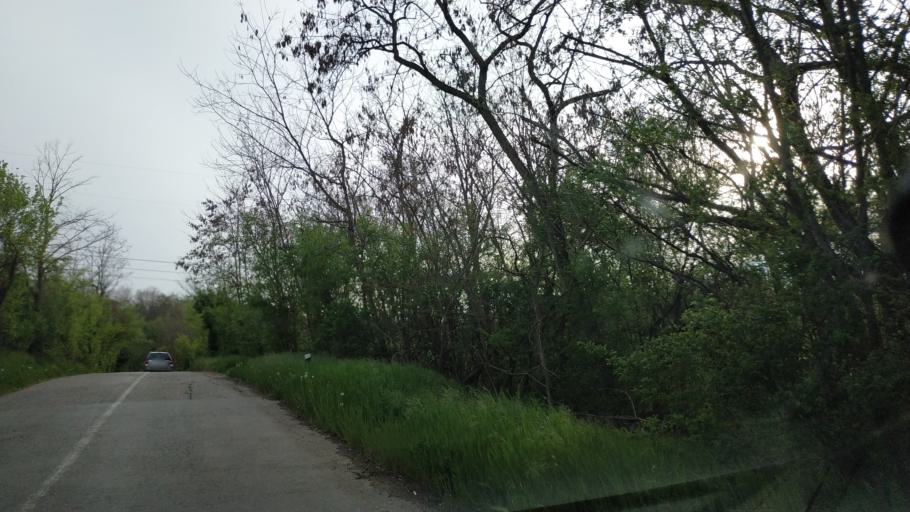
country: RS
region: Central Serbia
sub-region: Nisavski Okrug
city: Aleksinac
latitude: 43.4818
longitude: 21.8149
